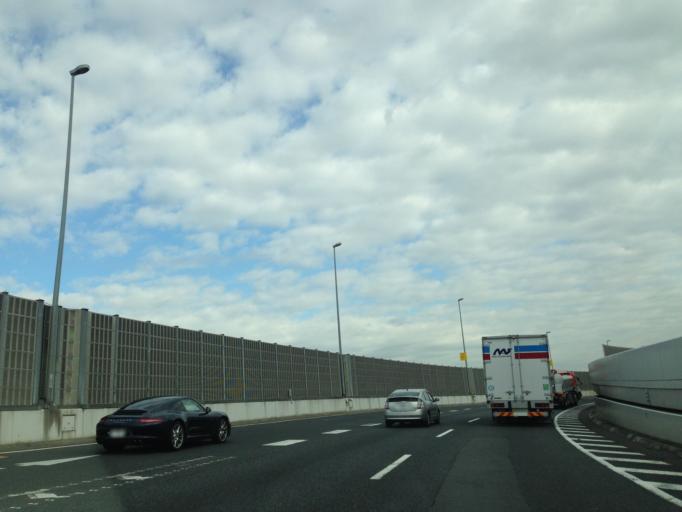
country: JP
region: Saitama
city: Kawaguchi
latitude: 35.7560
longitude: 139.7429
